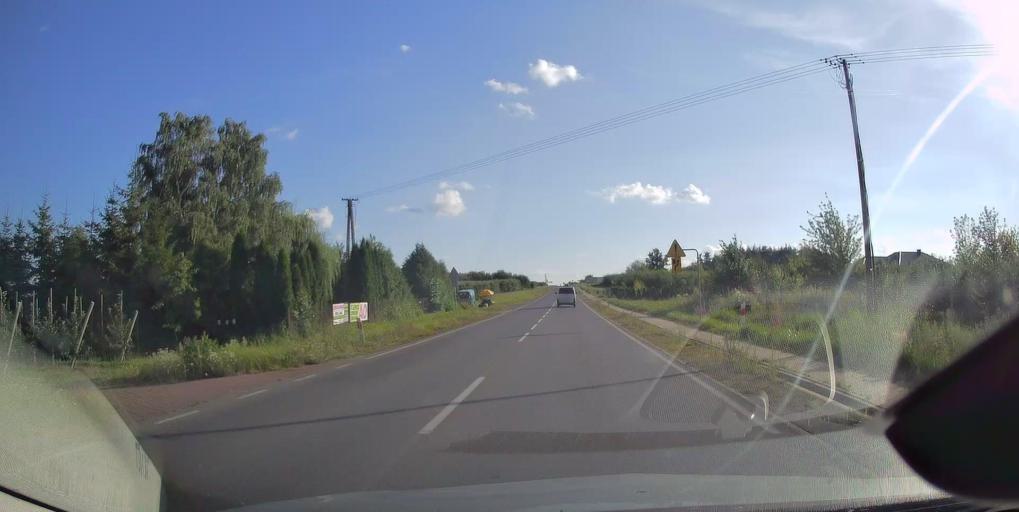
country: PL
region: Masovian Voivodeship
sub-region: Powiat grojecki
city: Belsk Duzy
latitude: 51.8426
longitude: 20.8310
